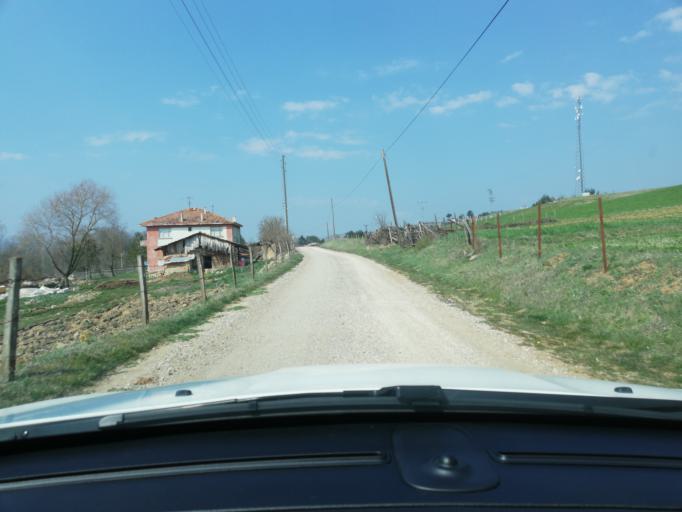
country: TR
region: Kastamonu
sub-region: Cide
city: Kastamonu
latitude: 41.4611
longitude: 33.7511
